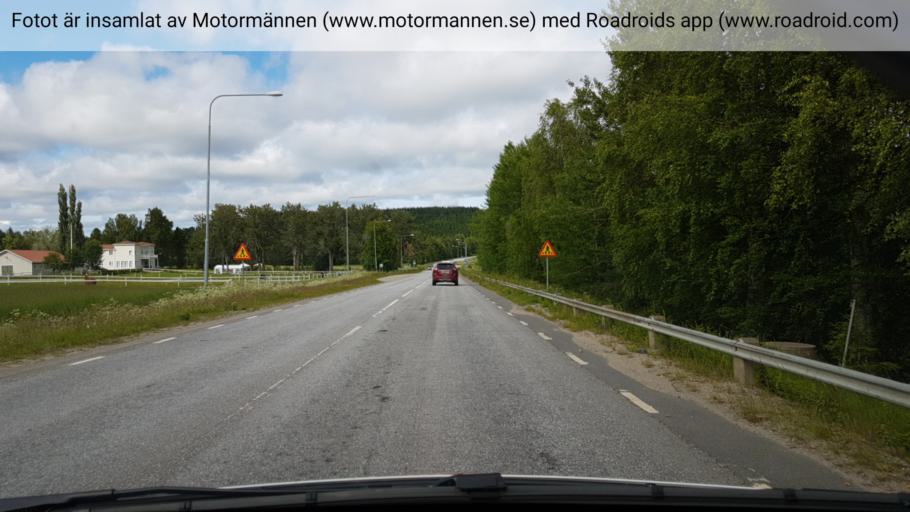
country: SE
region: Vaesterbotten
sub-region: Vannas Kommun
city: Vaennaes
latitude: 63.9156
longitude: 19.7753
